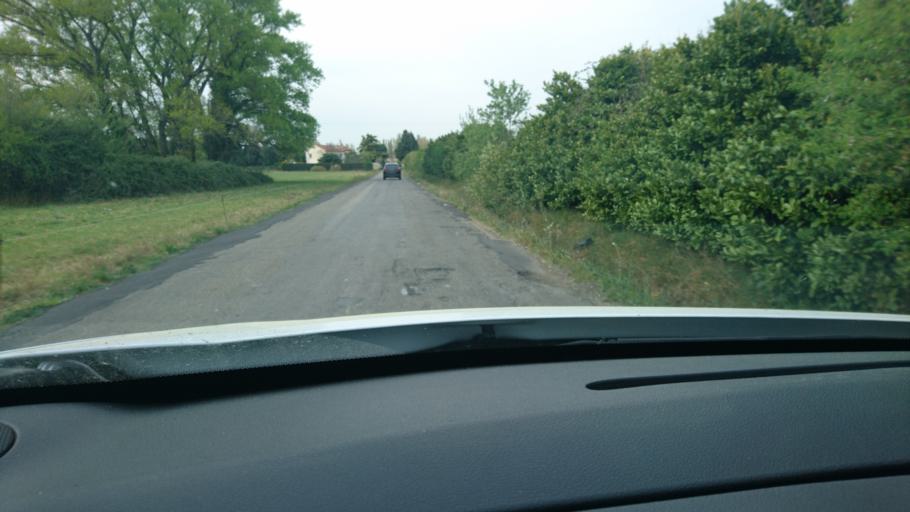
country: FR
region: Provence-Alpes-Cote d'Azur
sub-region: Departement du Vaucluse
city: Montfavet
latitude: 43.9496
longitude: 4.8816
